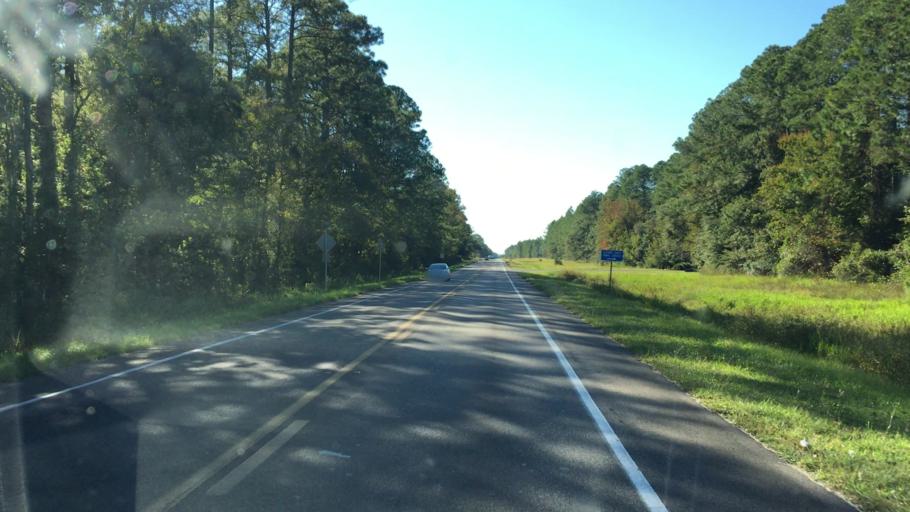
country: US
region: Florida
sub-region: Alachua County
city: Gainesville
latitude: 29.7030
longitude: -82.2800
